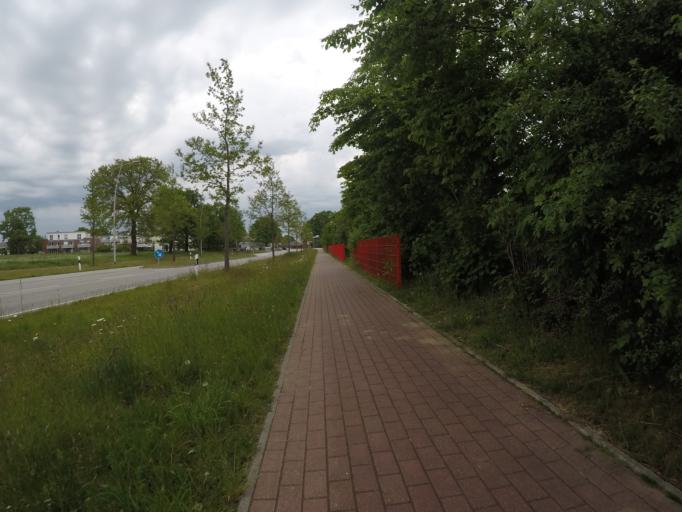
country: DE
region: Schleswig-Holstein
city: Norderstedt
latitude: 53.7319
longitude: 9.9854
